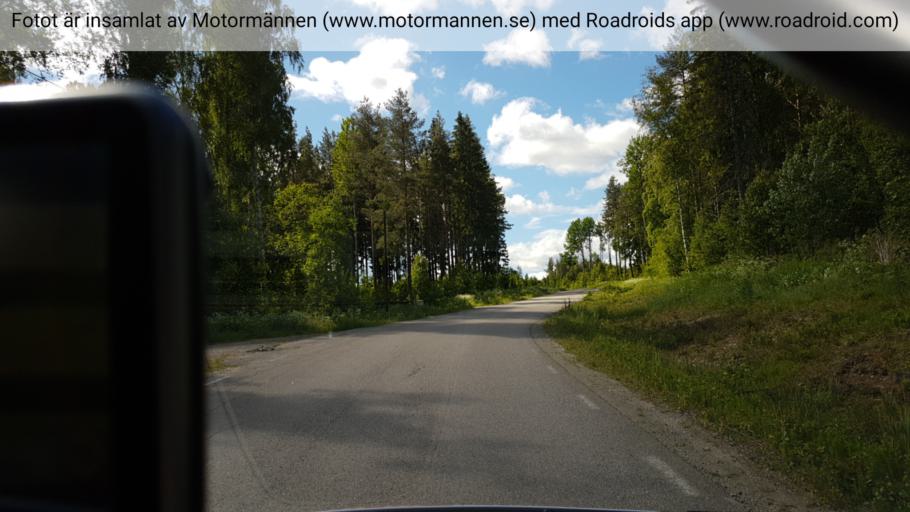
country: SE
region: Gaevleborg
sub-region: Hudiksvalls Kommun
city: Sorforsa
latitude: 61.6567
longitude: 16.9257
